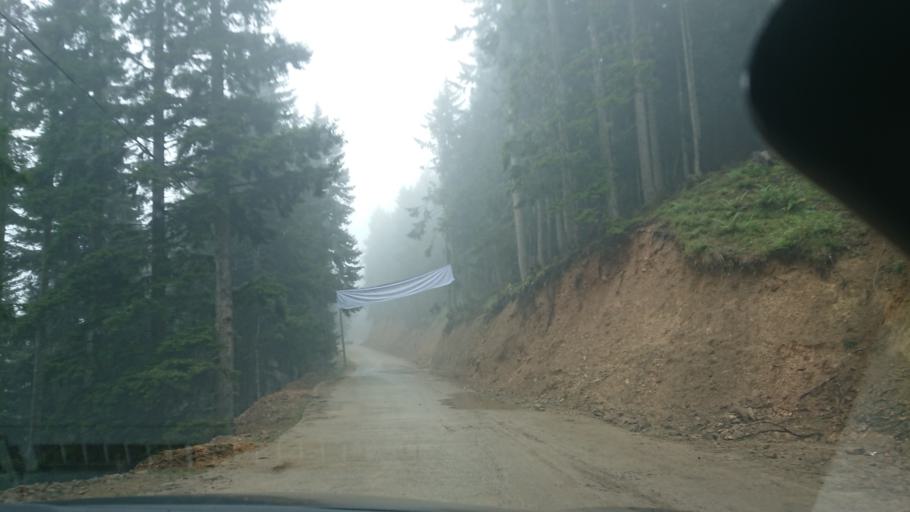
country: TR
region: Gumushane
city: Kurtun
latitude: 40.6708
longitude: 39.0006
